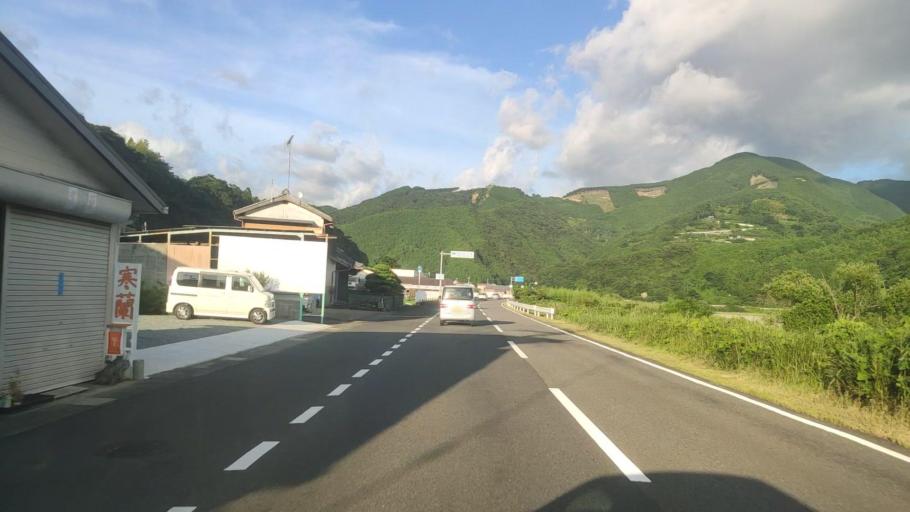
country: JP
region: Wakayama
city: Tanabe
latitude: 33.7186
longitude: 135.4750
